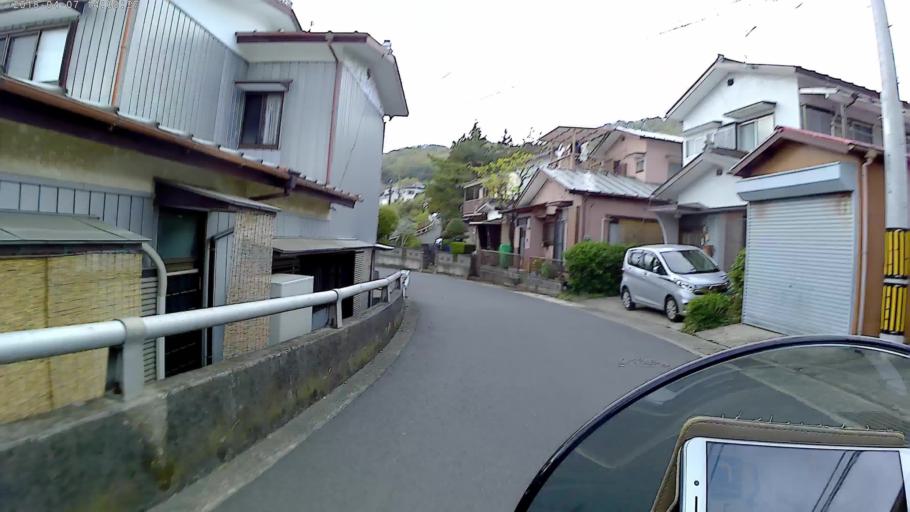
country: JP
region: Kanagawa
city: Hadano
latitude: 35.3664
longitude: 139.2458
